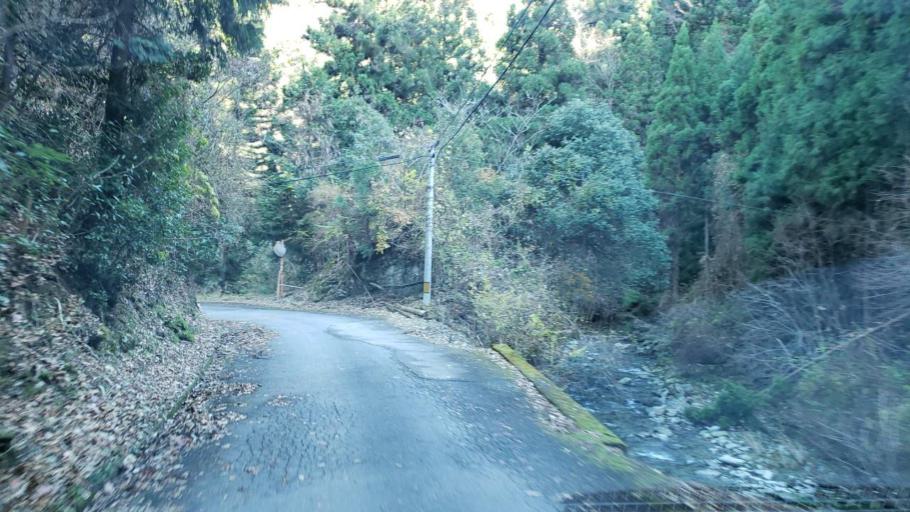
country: JP
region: Tokushima
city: Wakimachi
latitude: 33.9876
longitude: 133.9854
